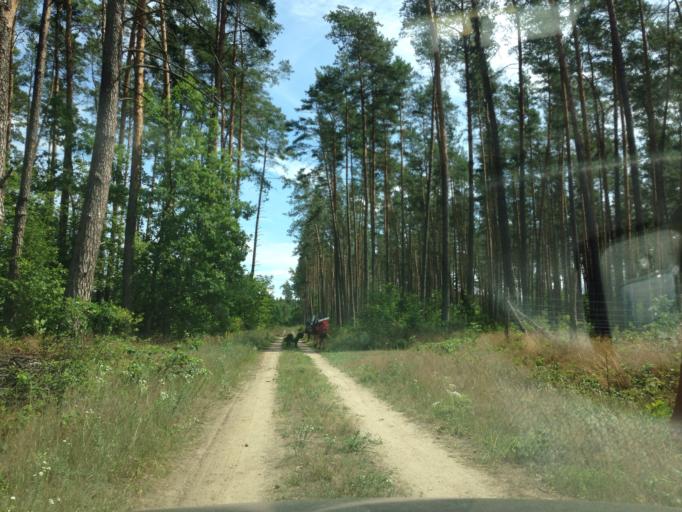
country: PL
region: Kujawsko-Pomorskie
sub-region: Powiat brodnicki
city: Bartniczka
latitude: 53.2810
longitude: 19.5681
